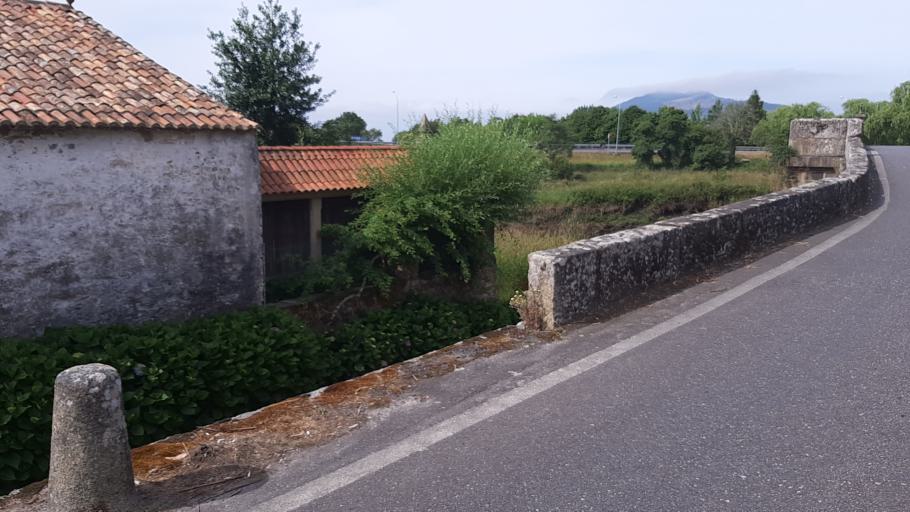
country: ES
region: Galicia
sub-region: Provincia de Pontevedra
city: O Rosal
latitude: 41.9152
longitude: -8.8273
